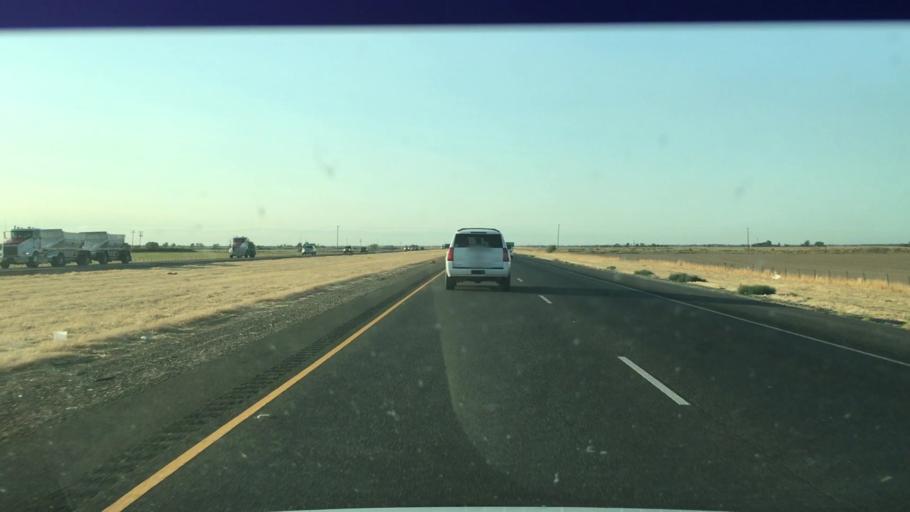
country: US
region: California
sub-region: Sacramento County
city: Laguna
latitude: 38.3501
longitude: -121.4714
